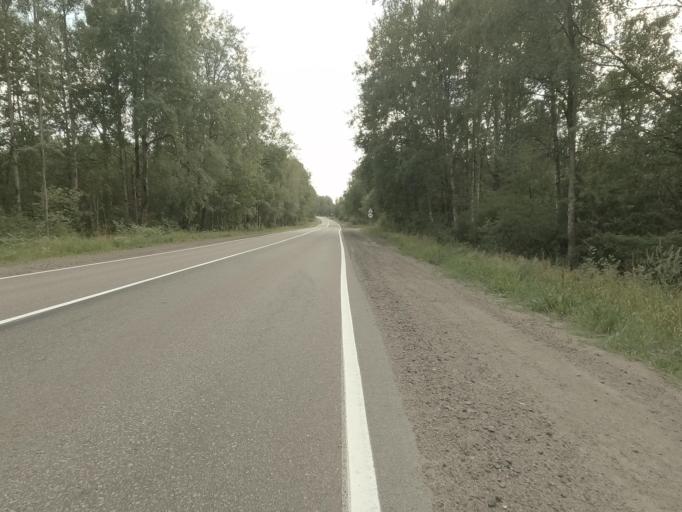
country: RU
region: Leningrad
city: Kamennogorsk
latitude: 60.8658
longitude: 28.9764
